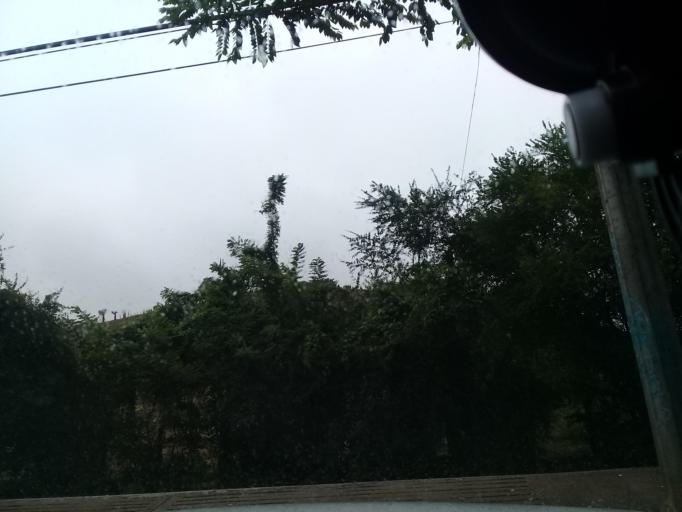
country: MX
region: Veracruz
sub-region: Chalma
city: San Pedro Coyutla
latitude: 21.2238
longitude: -98.4324
